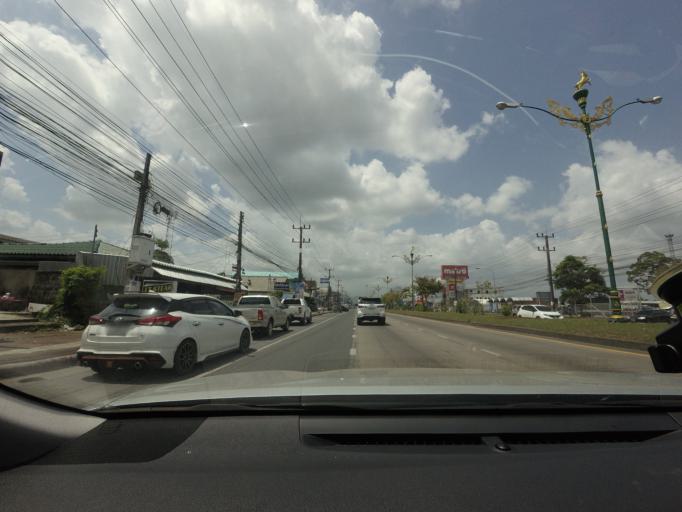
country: TH
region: Nakhon Si Thammarat
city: Nakhon Si Thammarat
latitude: 8.4341
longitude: 99.9288
